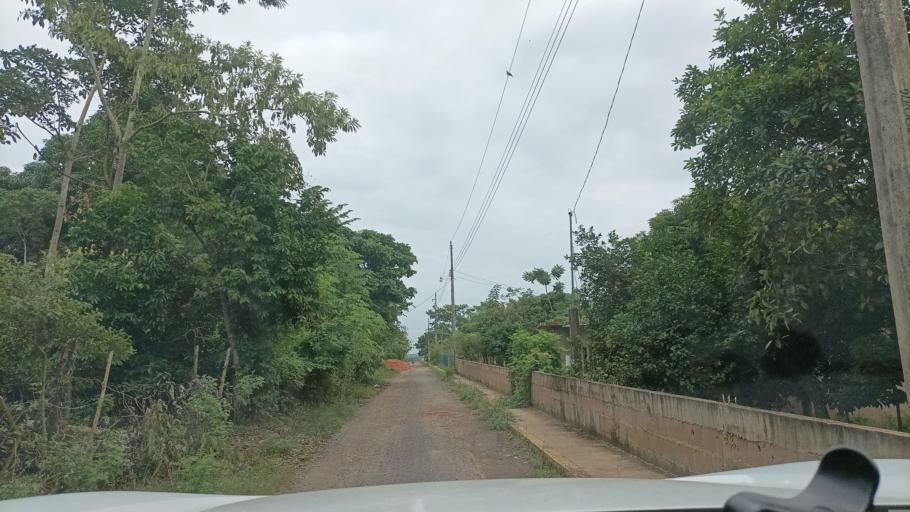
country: MX
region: Veracruz
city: Oteapan
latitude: 17.9884
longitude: -94.6746
